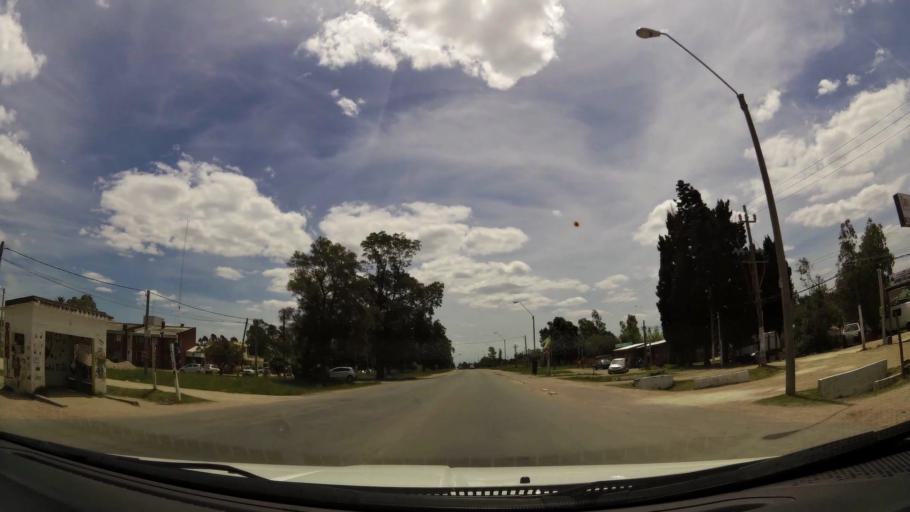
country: UY
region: San Jose
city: Delta del Tigre
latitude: -34.7498
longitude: -56.4191
